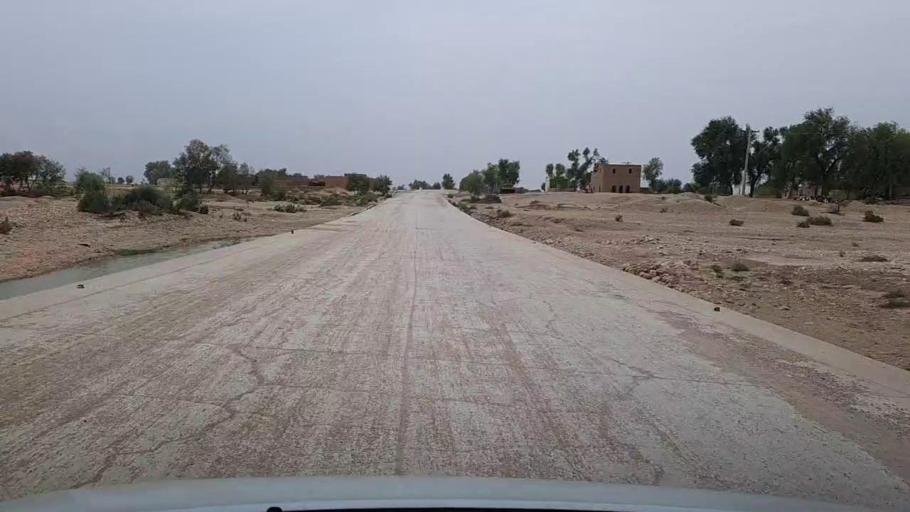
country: PK
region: Sindh
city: Sehwan
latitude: 26.3186
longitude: 67.7392
